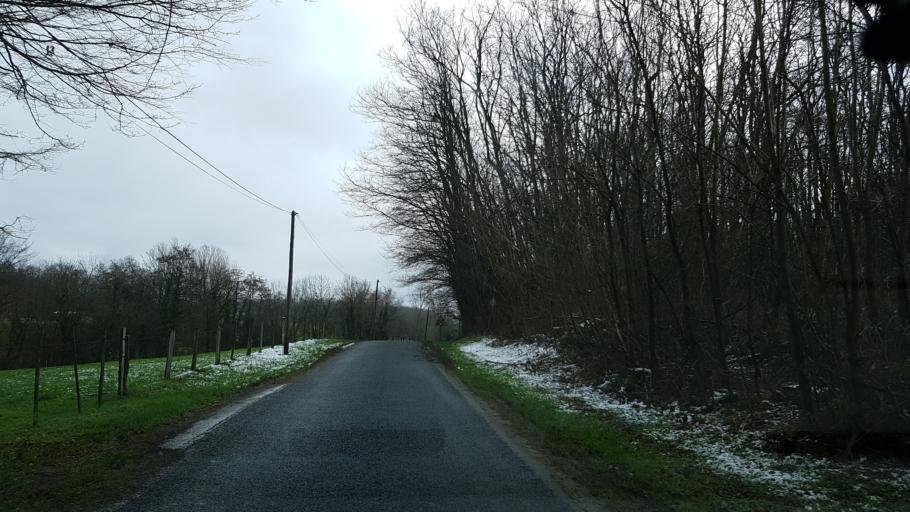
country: FR
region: Rhone-Alpes
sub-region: Departement de l'Ain
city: Buellas
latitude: 46.1863
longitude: 5.1525
